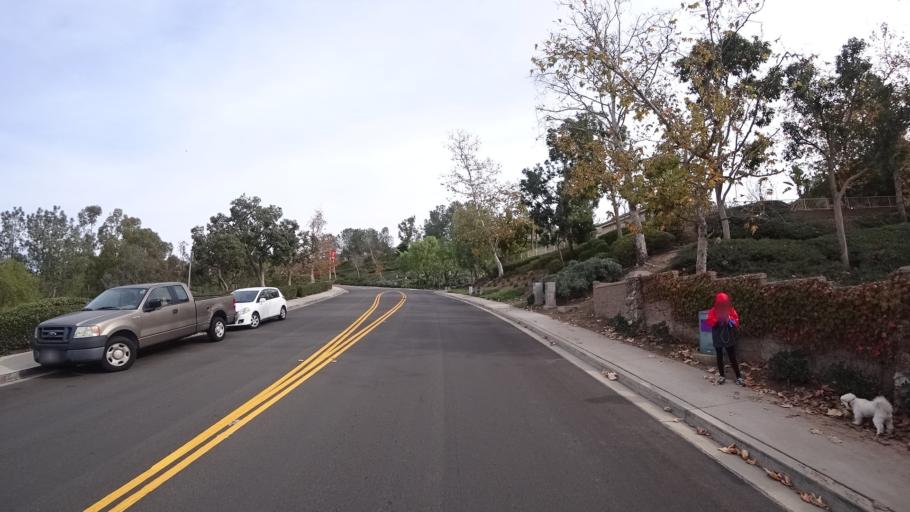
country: US
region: California
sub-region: Orange County
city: Laguna Woods
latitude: 33.6008
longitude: -117.7409
